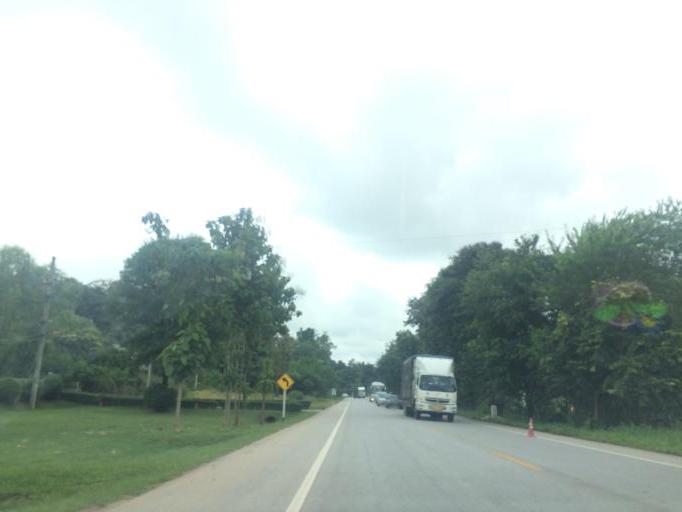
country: TH
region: Chiang Rai
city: Mae Lao
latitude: 19.7469
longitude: 99.6830
